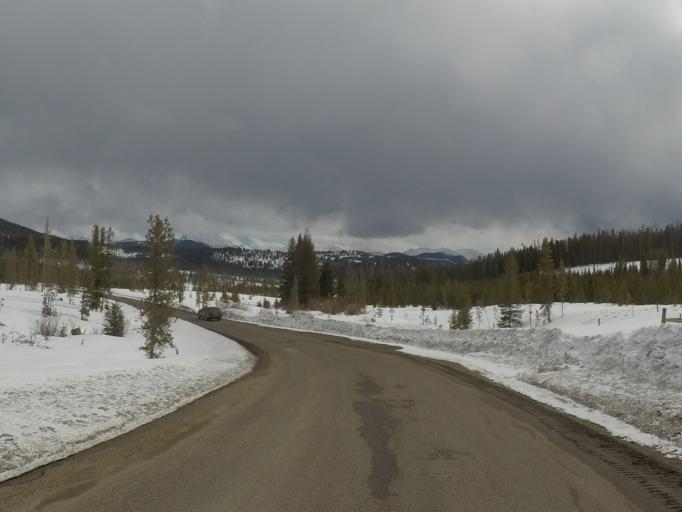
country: US
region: Montana
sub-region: Granite County
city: Philipsburg
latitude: 46.2132
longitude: -113.2575
